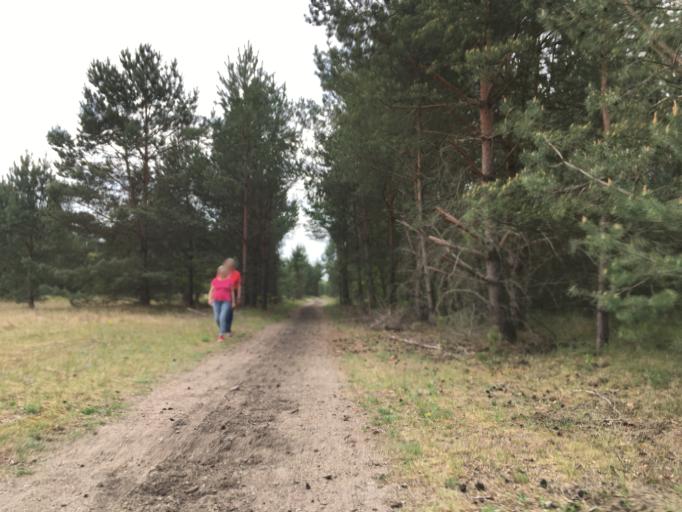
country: DE
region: Brandenburg
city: Rudnitz
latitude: 52.6980
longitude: 13.6150
